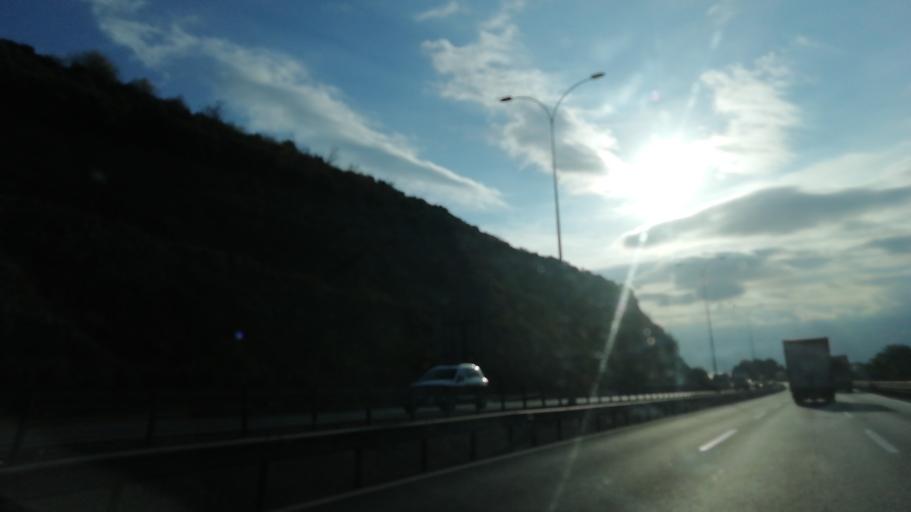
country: TR
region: Kocaeli
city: Hereke
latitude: 40.7810
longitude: 29.6285
